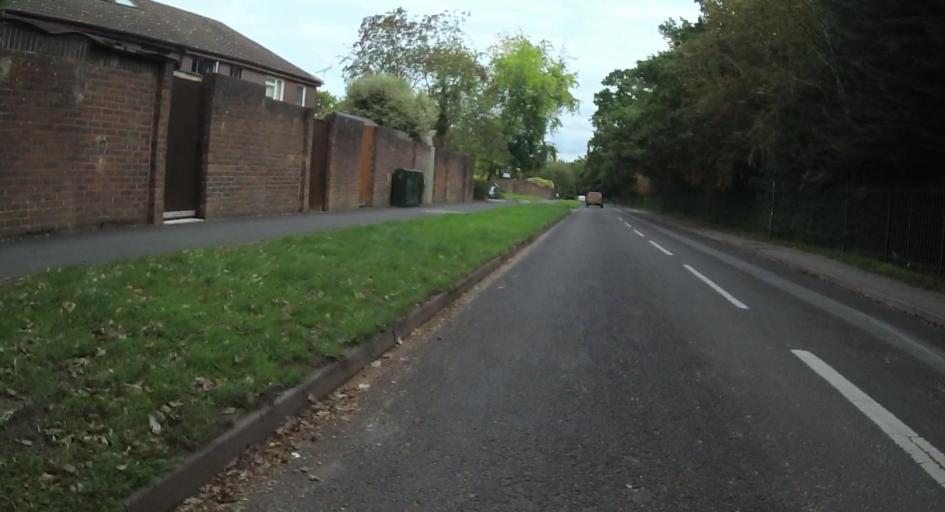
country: GB
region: England
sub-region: Surrey
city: Knaphill
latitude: 51.3152
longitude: -0.6050
